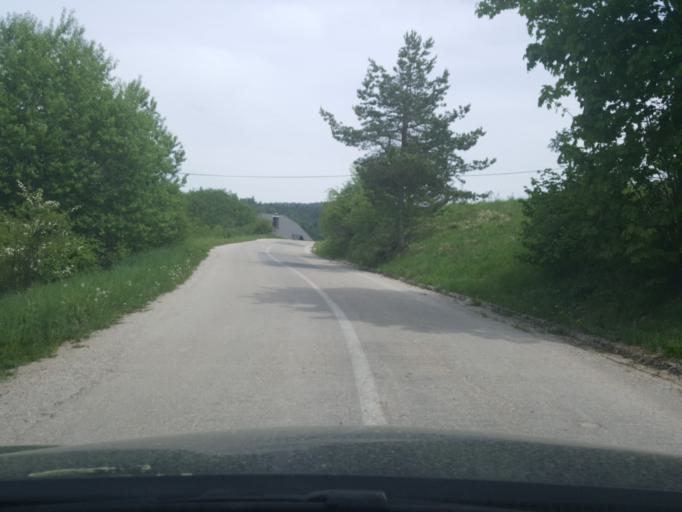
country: RS
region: Central Serbia
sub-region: Zlatiborski Okrug
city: Bajina Basta
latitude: 43.8950
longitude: 19.5201
